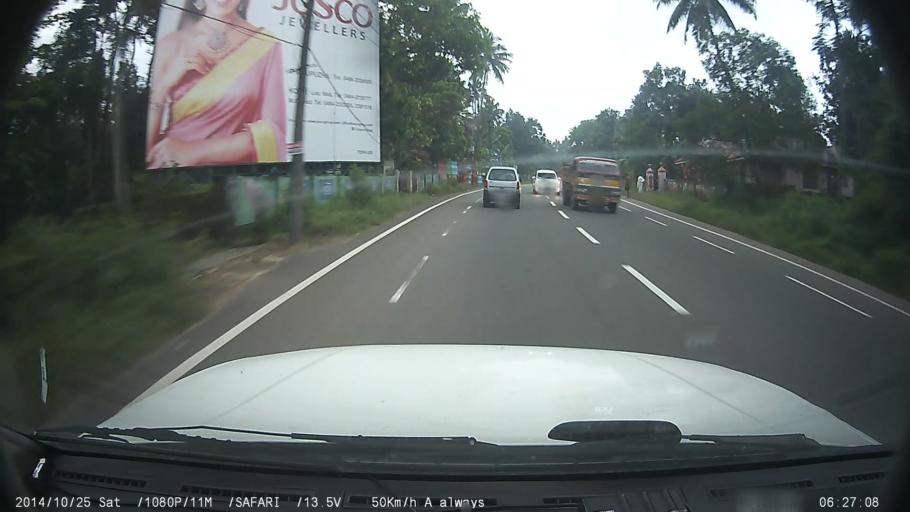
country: IN
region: Kerala
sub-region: Ernakulam
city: Perumbavoor
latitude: 10.0574
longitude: 76.5290
